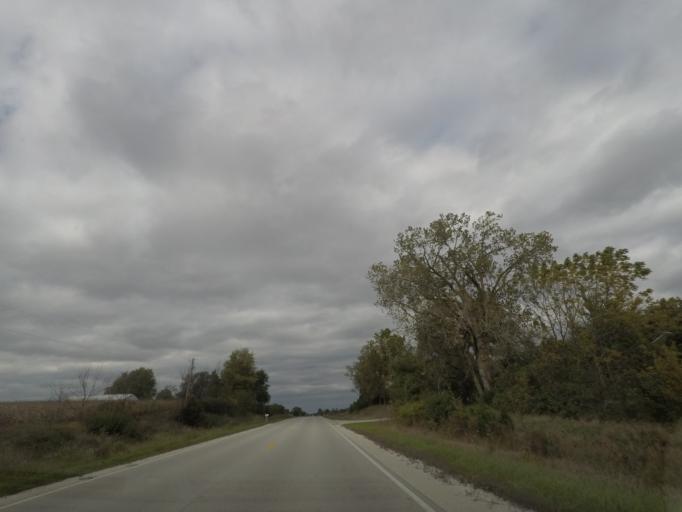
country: US
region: Iowa
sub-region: Story County
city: Huxley
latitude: 41.8690
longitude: -93.5315
